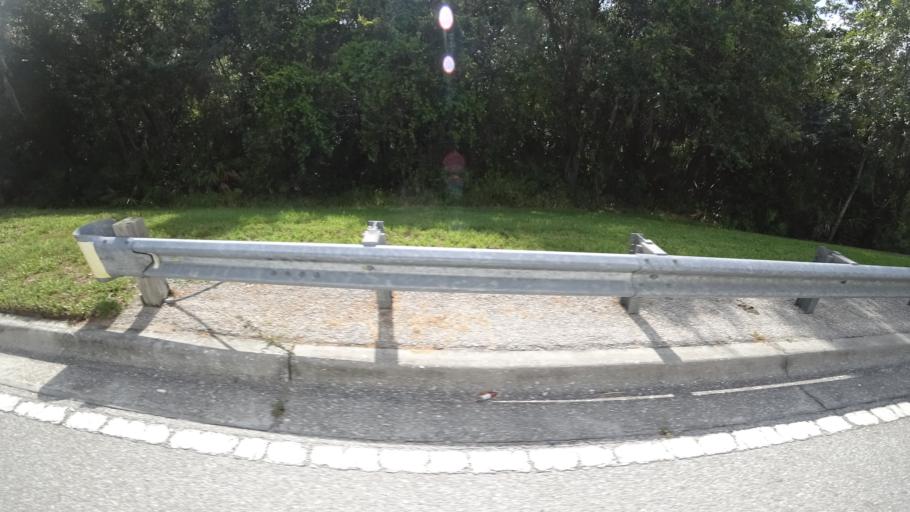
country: US
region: Florida
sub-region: Sarasota County
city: The Meadows
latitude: 27.4068
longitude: -82.4503
